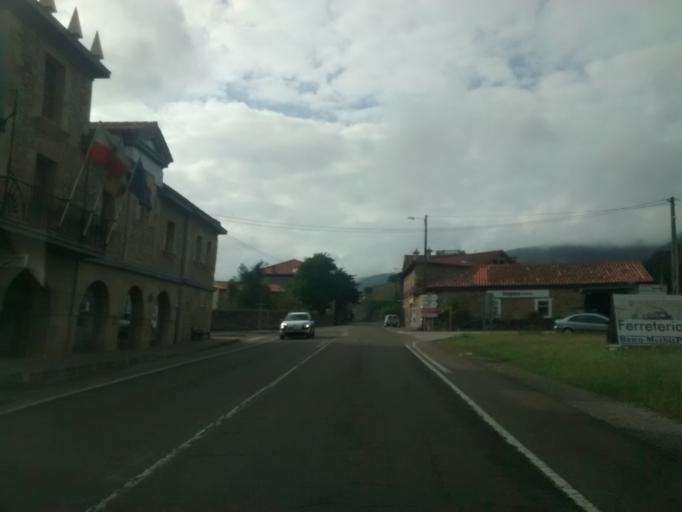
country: ES
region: Cantabria
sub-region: Provincia de Cantabria
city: Santiurde de Toranzo
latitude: 43.2128
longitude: -3.9395
